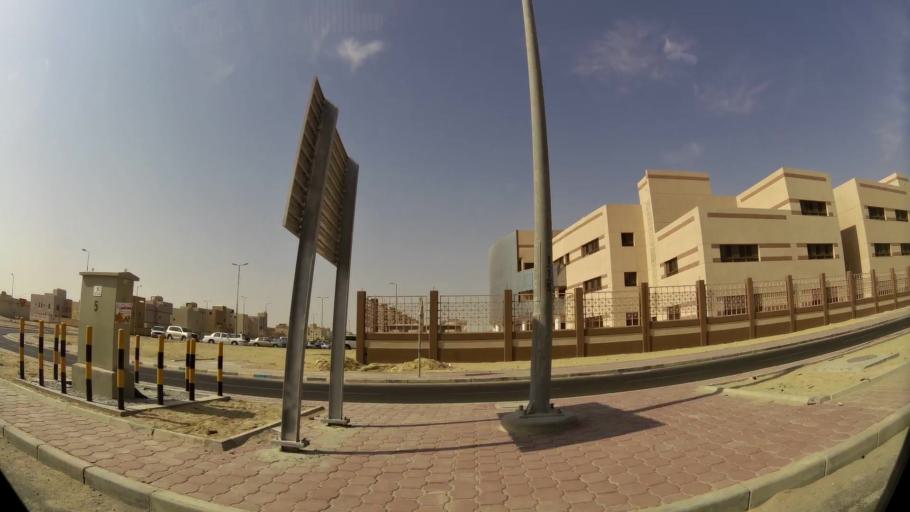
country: KW
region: Al Ahmadi
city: Al Wafrah
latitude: 28.7984
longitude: 48.0716
